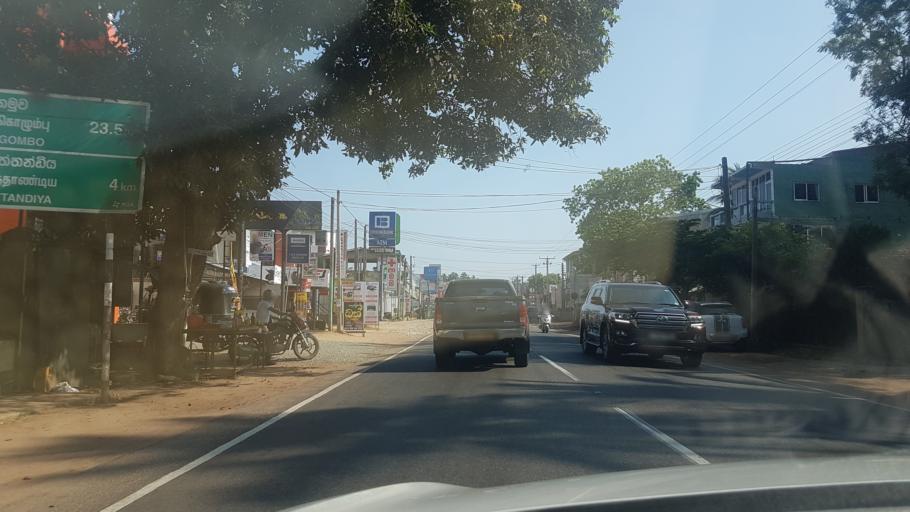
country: LK
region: North Western
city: Chilaw
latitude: 7.4151
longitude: 79.8307
